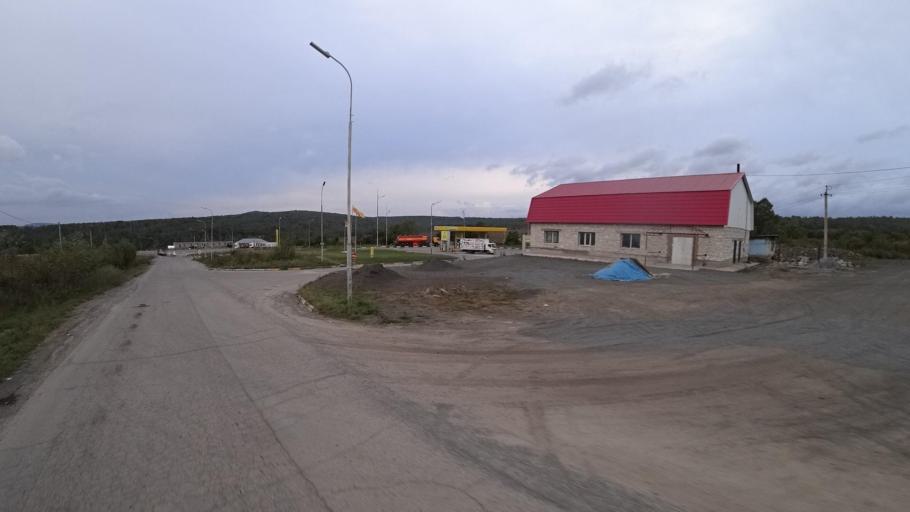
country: RU
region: Jewish Autonomous Oblast
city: Izvestkovyy
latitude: 48.9709
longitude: 131.5547
